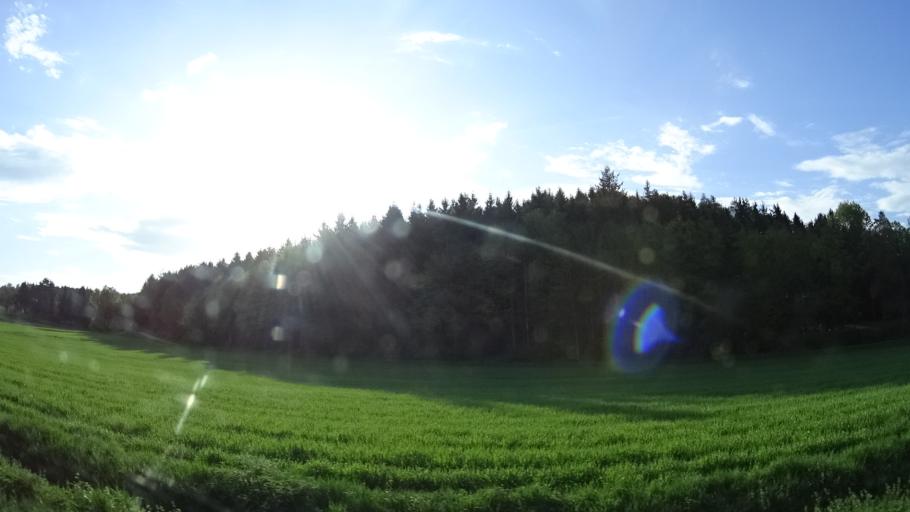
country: DE
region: Baden-Wuerttemberg
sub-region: Freiburg Region
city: Dietingen
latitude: 48.2120
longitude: 8.6534
